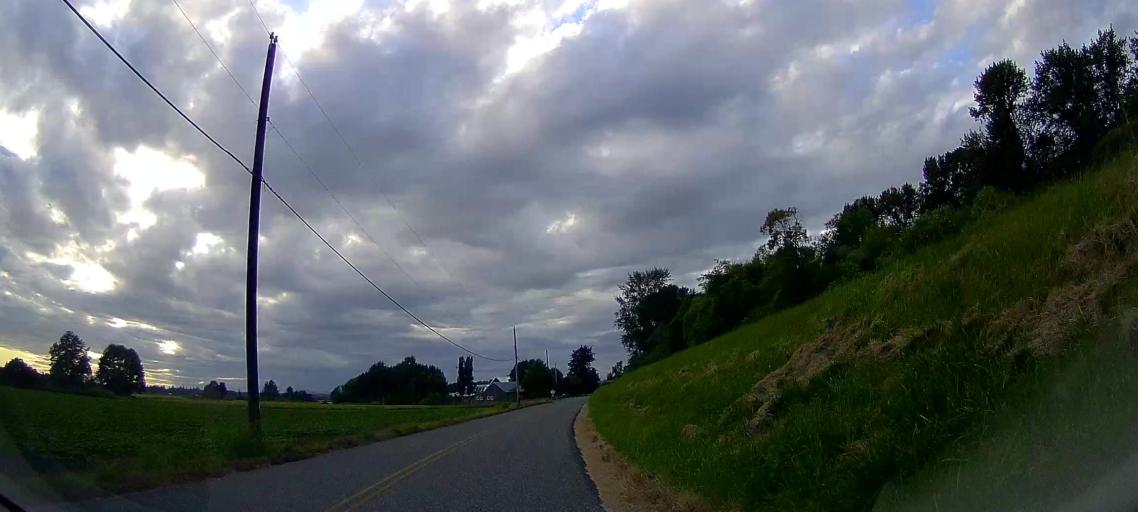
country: US
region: Washington
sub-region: Skagit County
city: Mount Vernon
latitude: 48.3433
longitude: -122.3551
